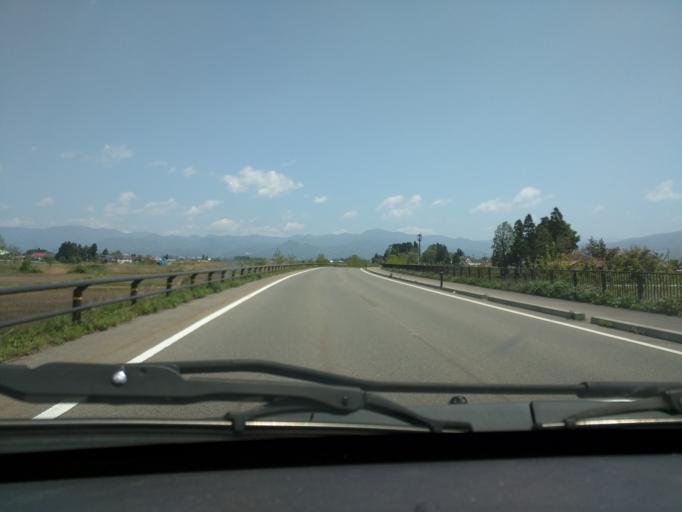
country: JP
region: Fukushima
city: Kitakata
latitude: 37.6021
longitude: 139.8433
